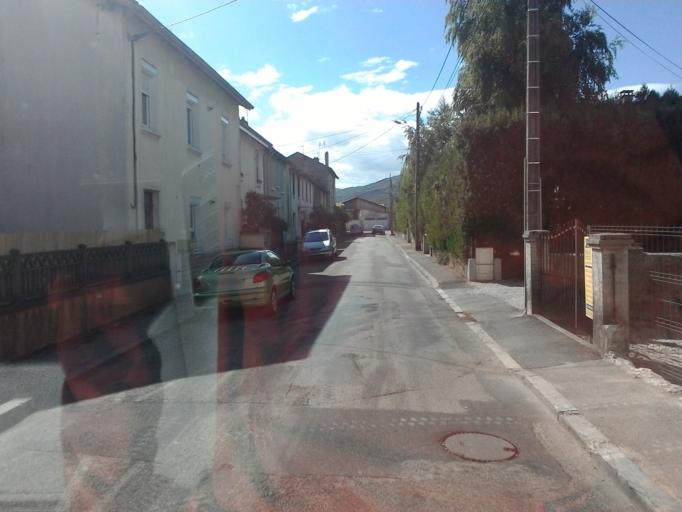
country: FR
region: Rhone-Alpes
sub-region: Departement de l'Ain
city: Amberieu-en-Bugey
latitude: 45.9574
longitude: 5.3543
